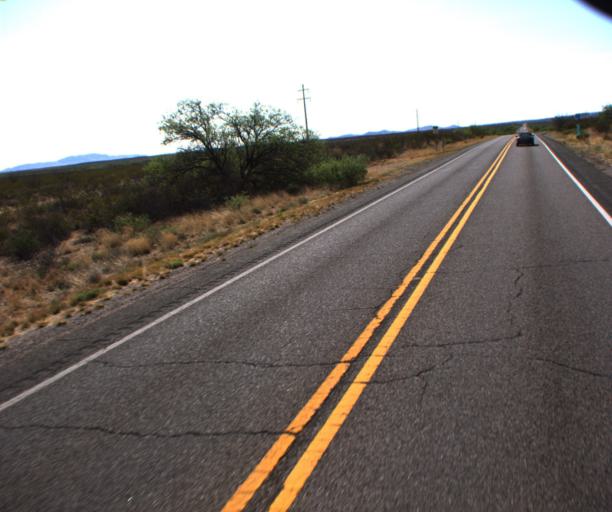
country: US
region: Arizona
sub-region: Cochise County
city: Tombstone
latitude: 31.7682
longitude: -110.1215
